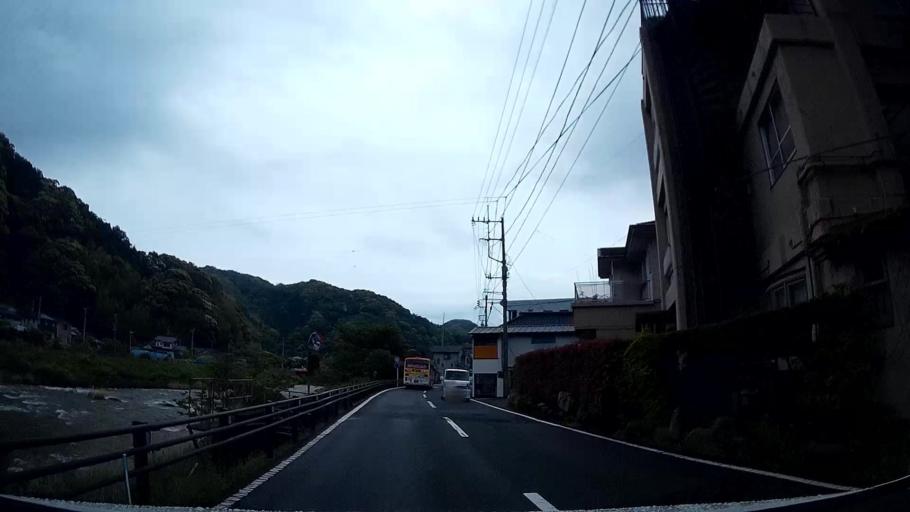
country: JP
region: Shizuoka
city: Shimoda
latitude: 34.7642
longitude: 138.9780
